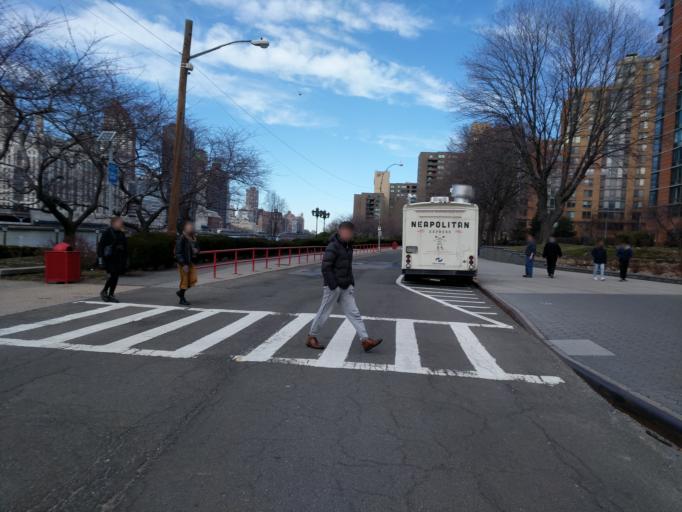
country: US
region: New York
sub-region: Queens County
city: Long Island City
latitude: 40.7593
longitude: -73.9534
